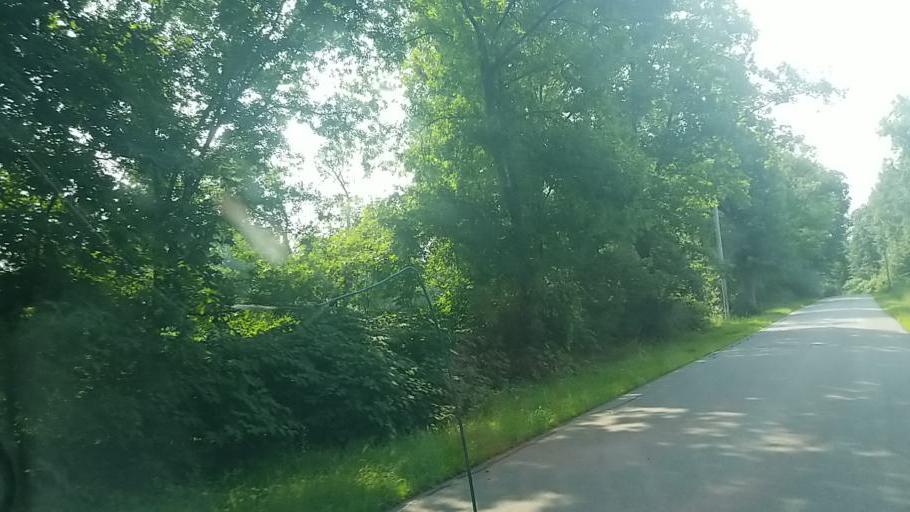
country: US
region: New York
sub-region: Montgomery County
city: Fonda
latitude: 42.9290
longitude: -74.4476
